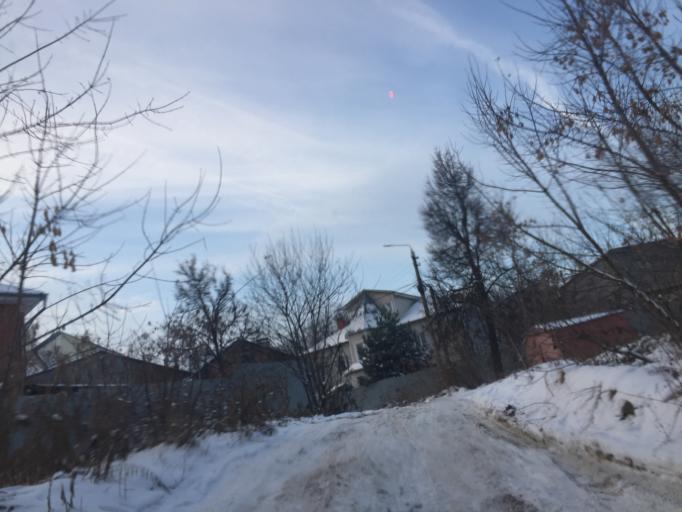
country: RU
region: Tula
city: Tula
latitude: 54.2027
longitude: 37.6633
